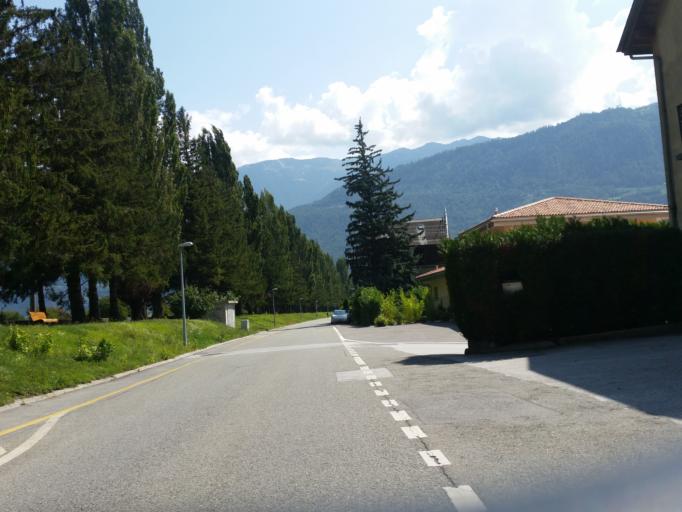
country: CH
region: Valais
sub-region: Conthey District
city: Ardon
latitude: 46.2135
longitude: 7.2633
